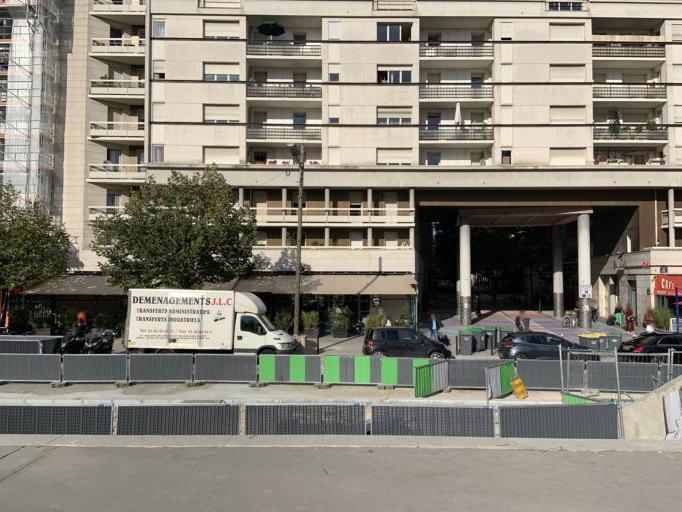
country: FR
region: Ile-de-France
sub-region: Departement du Val-de-Marne
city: Ivry-sur-Seine
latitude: 48.8391
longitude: 2.3803
